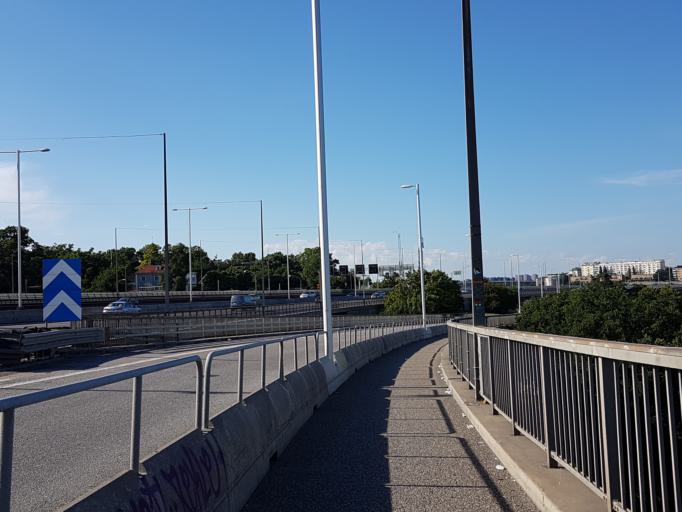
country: SE
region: Stockholm
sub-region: Solna Kommun
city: Solna
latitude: 59.3199
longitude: 17.9974
